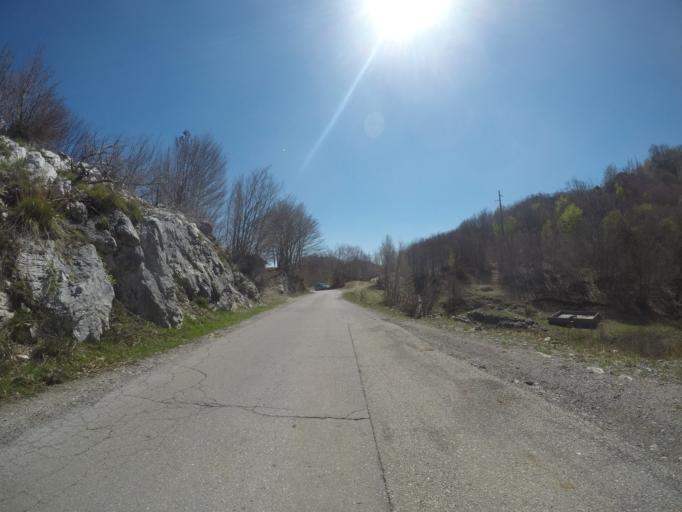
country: ME
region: Cetinje
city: Cetinje
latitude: 42.4350
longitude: 18.8641
